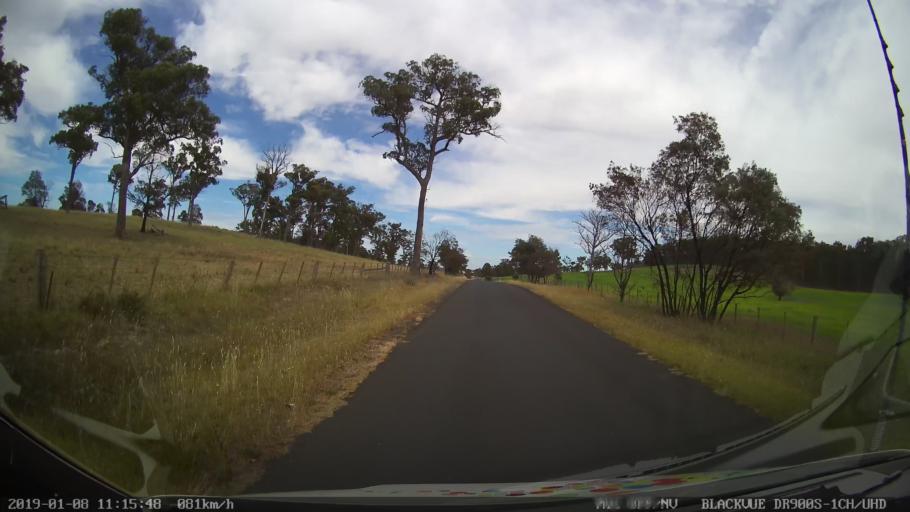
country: AU
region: New South Wales
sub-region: Guyra
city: Guyra
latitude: -30.2219
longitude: 151.5725
